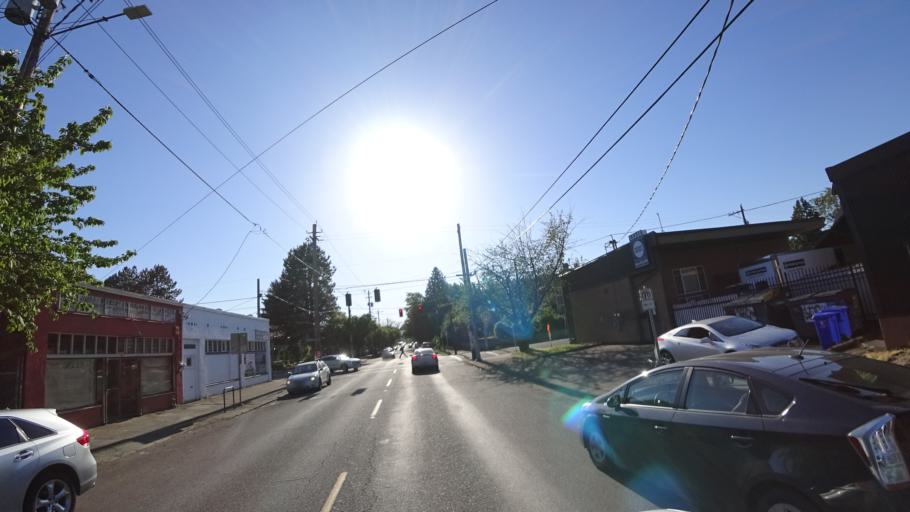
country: US
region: Oregon
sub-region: Multnomah County
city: Portland
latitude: 45.5590
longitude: -122.6746
